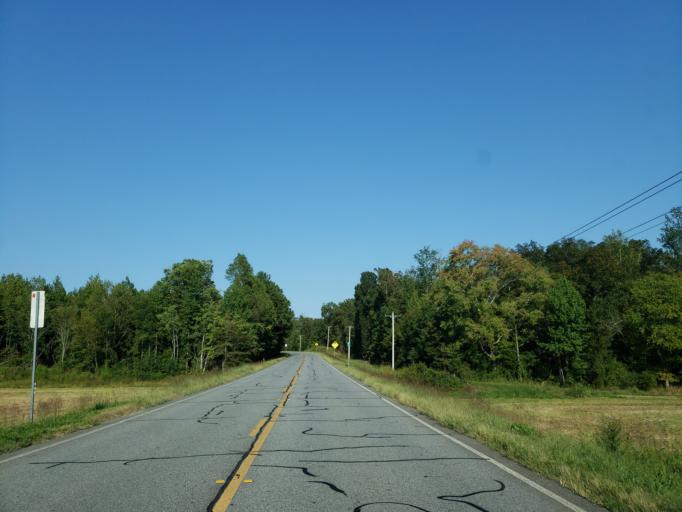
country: US
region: Georgia
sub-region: Whitfield County
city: Varnell
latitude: 34.9086
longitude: -84.8723
